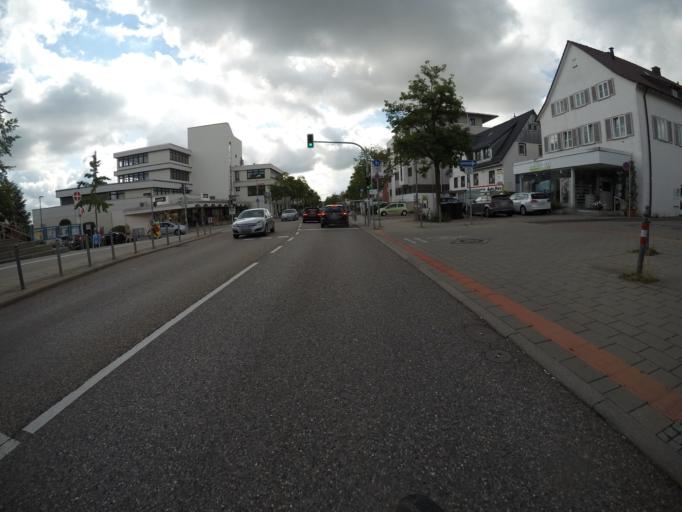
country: DE
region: Baden-Wuerttemberg
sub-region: Regierungsbezirk Stuttgart
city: Ostfildern
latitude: 48.7441
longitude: 9.2137
